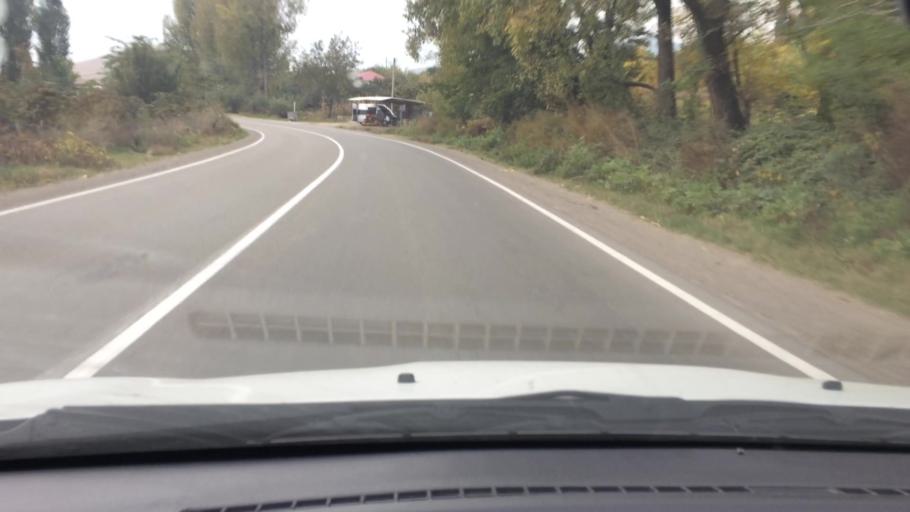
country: AM
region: Tavush
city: Bagratashen
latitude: 41.2941
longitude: 44.7880
